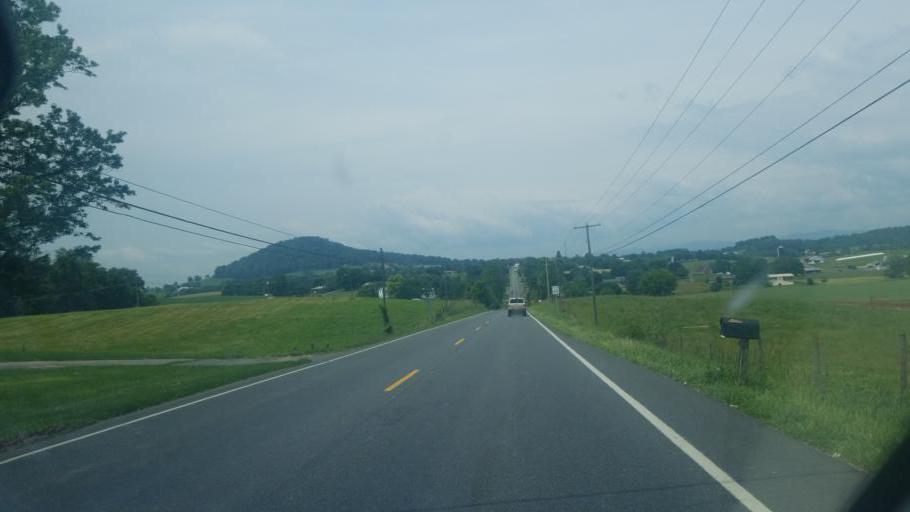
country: US
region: Virginia
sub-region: Rockingham County
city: Dayton
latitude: 38.4538
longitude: -78.9246
